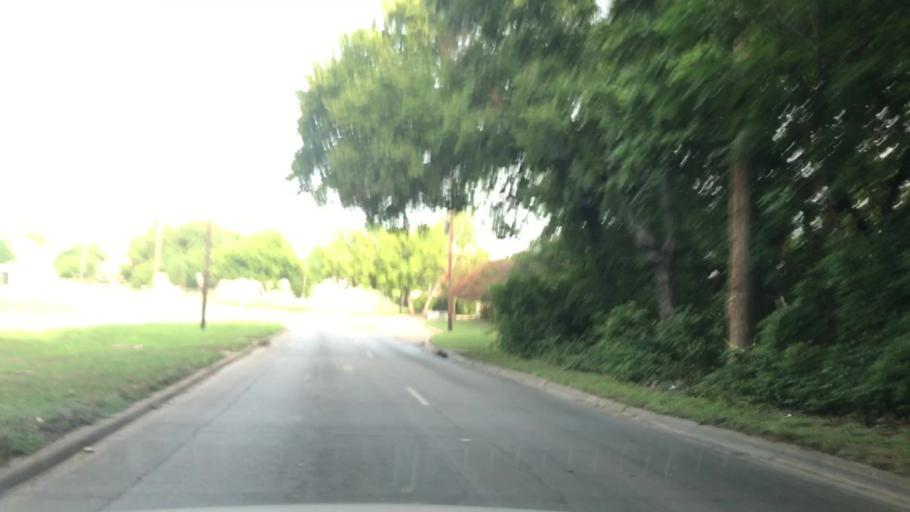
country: US
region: Texas
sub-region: Dallas County
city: Dallas
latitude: 32.7837
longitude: -96.7333
